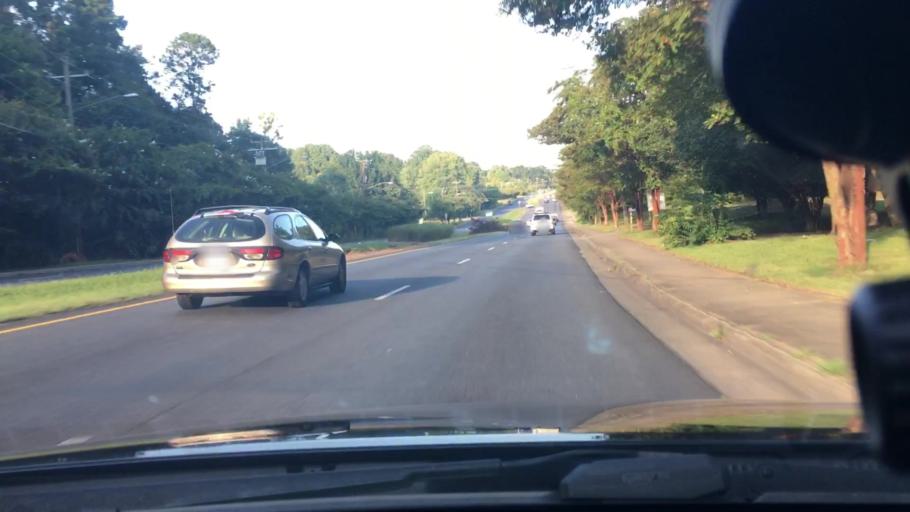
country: US
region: North Carolina
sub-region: Mecklenburg County
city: Mint Hill
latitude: 35.2089
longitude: -80.7059
